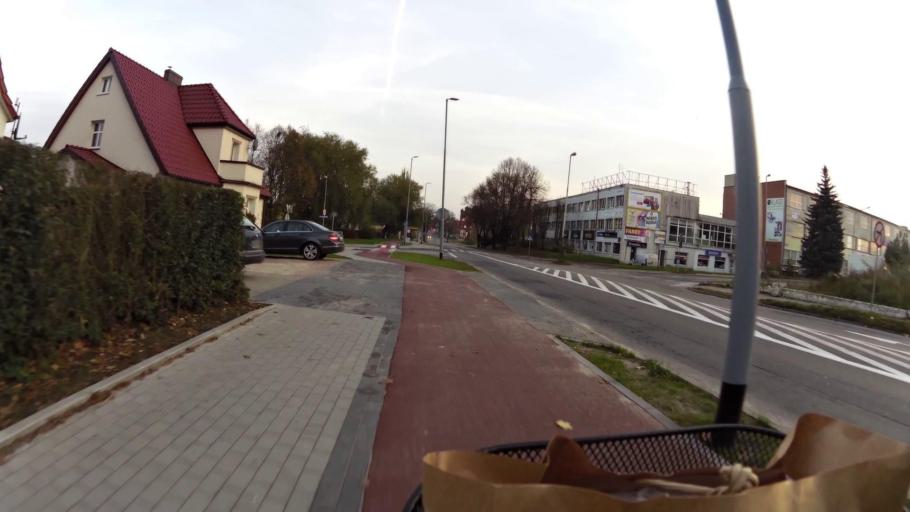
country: PL
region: West Pomeranian Voivodeship
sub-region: Koszalin
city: Koszalin
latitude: 54.1990
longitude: 16.1645
